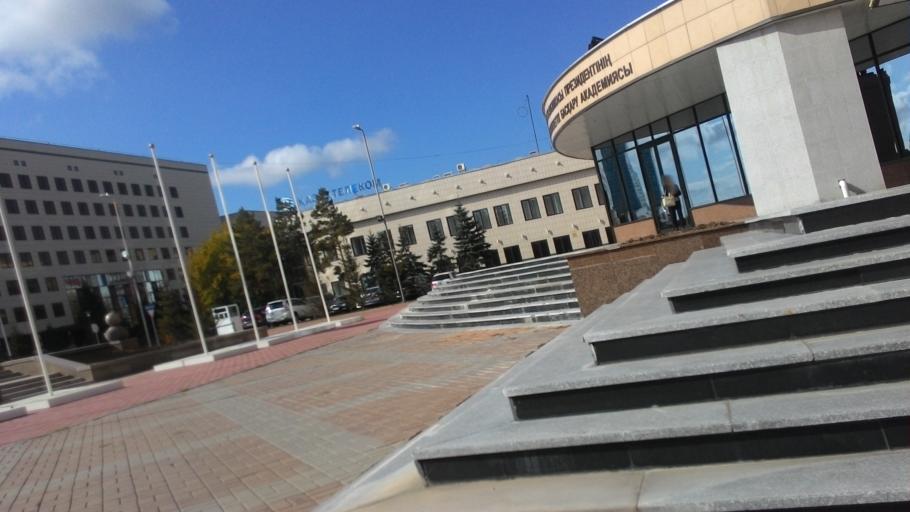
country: KZ
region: Astana Qalasy
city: Astana
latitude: 51.1681
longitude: 71.4205
